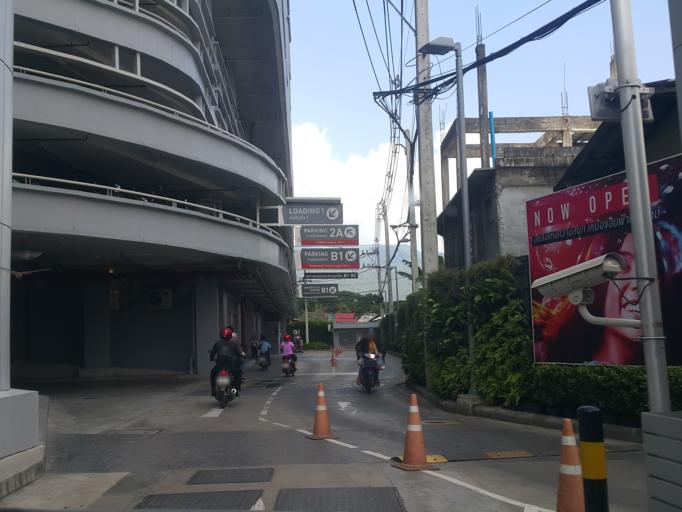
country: TH
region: Chiang Mai
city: Chiang Mai
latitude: 18.8026
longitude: 98.9677
